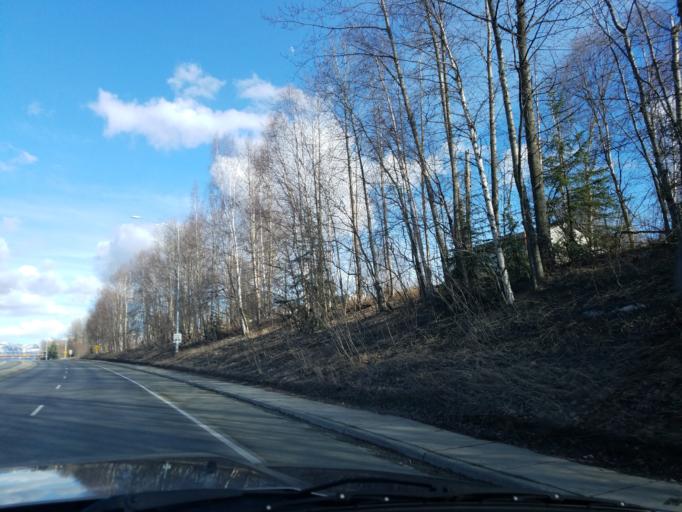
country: US
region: Alaska
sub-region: Anchorage Municipality
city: Anchorage
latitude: 61.1805
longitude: -149.9109
